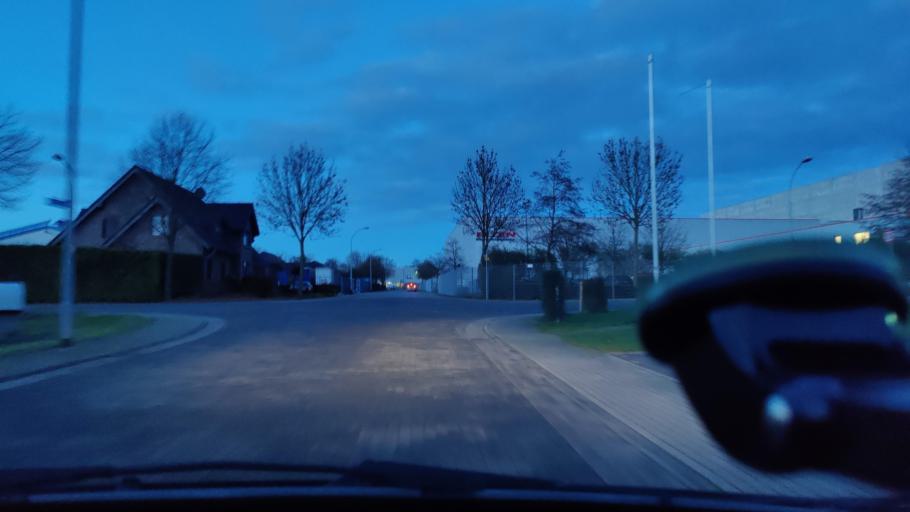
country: DE
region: North Rhine-Westphalia
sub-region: Regierungsbezirk Dusseldorf
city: Uedem
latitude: 51.6582
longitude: 6.2701
